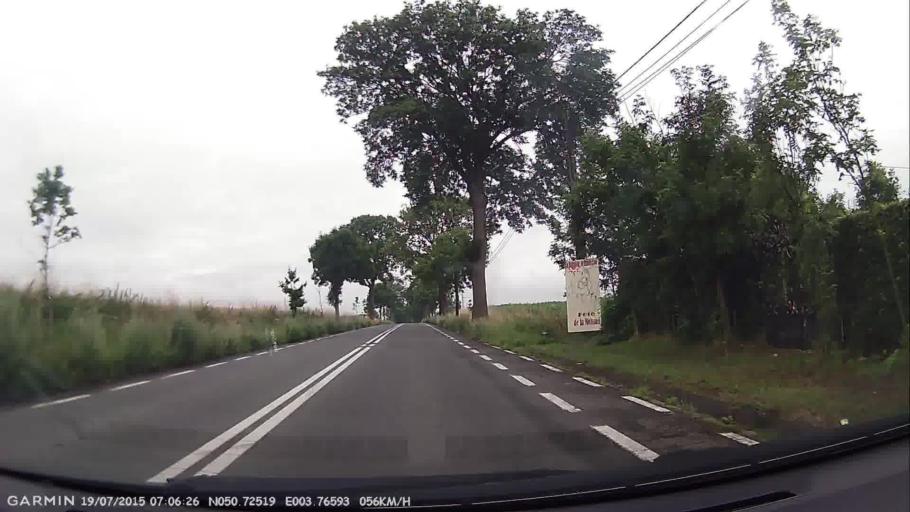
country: BE
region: Wallonia
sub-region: Province du Hainaut
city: Flobecq
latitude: 50.7253
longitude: 3.7657
